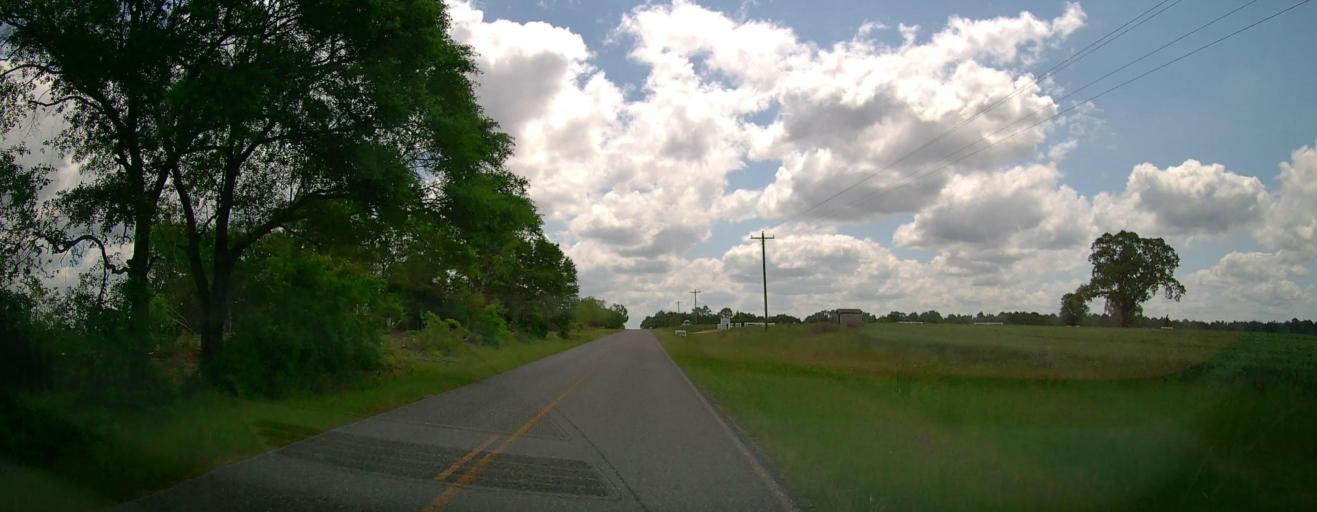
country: US
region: Georgia
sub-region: Dodge County
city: Chester
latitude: 32.5443
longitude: -83.1371
